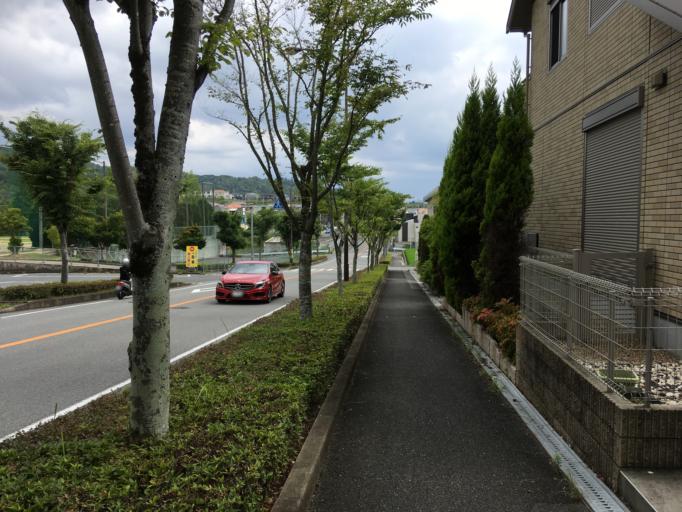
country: JP
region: Nara
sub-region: Ikoma-shi
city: Ikoma
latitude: 34.6738
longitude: 135.7187
